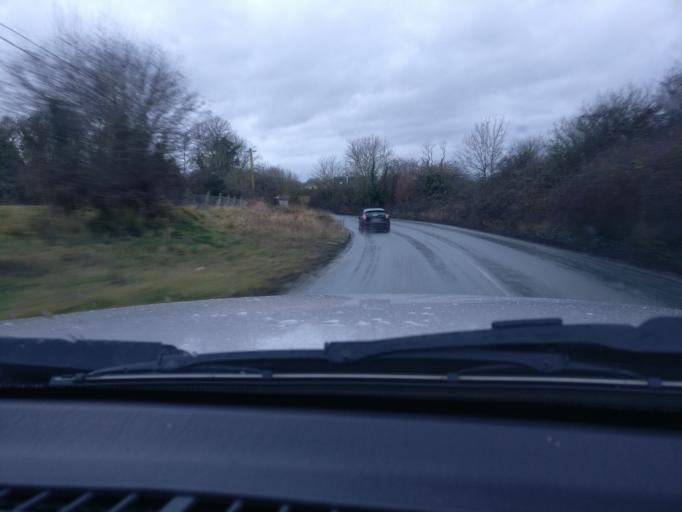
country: IE
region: Leinster
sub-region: An Mhi
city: Longwood
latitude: 53.4536
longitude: -6.9443
